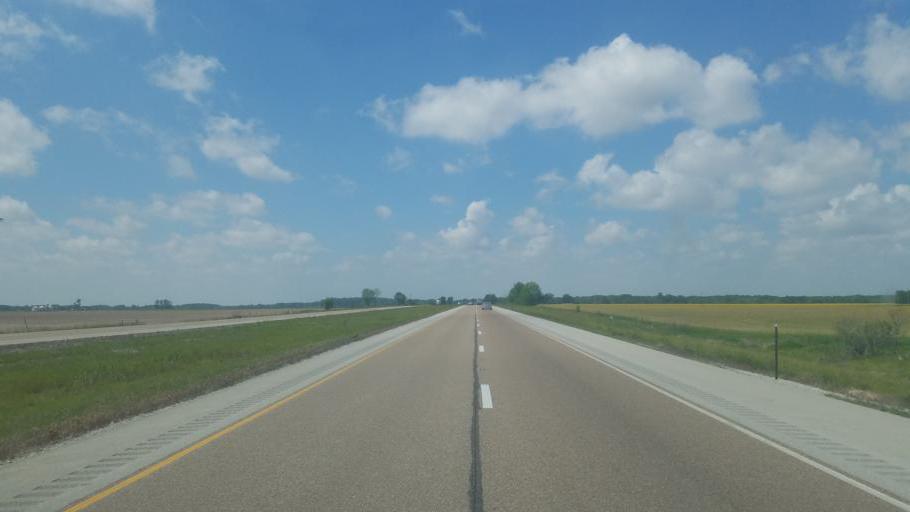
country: US
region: Illinois
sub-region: Clark County
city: Casey
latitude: 39.2978
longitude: -88.0299
